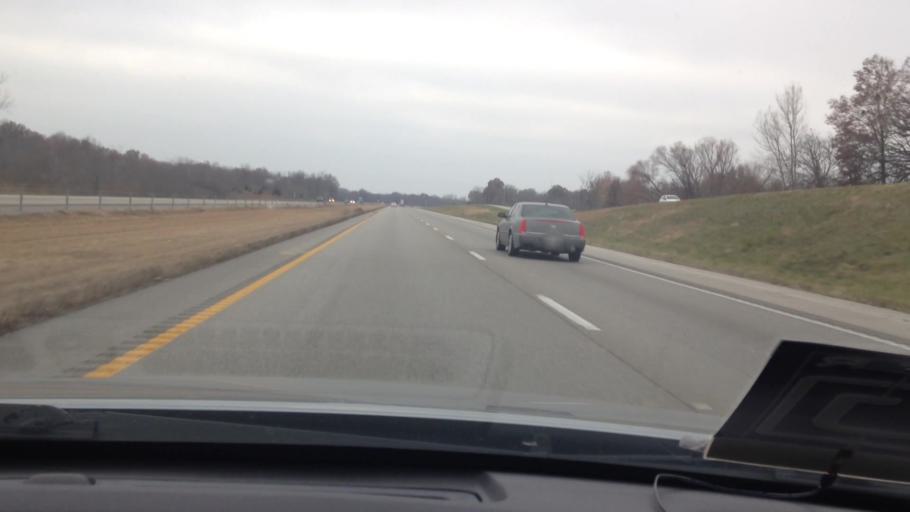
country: US
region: Missouri
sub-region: Cass County
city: Harrisonville
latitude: 38.6724
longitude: -94.4111
